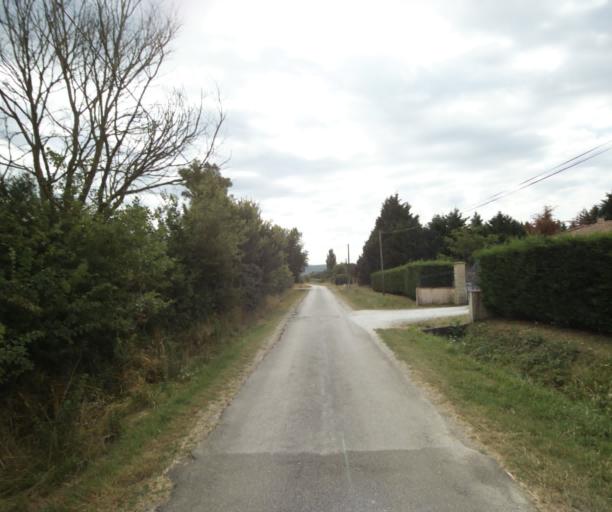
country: FR
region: Midi-Pyrenees
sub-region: Departement de la Haute-Garonne
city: Saint-Felix-Lauragais
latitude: 43.4322
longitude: 1.9410
